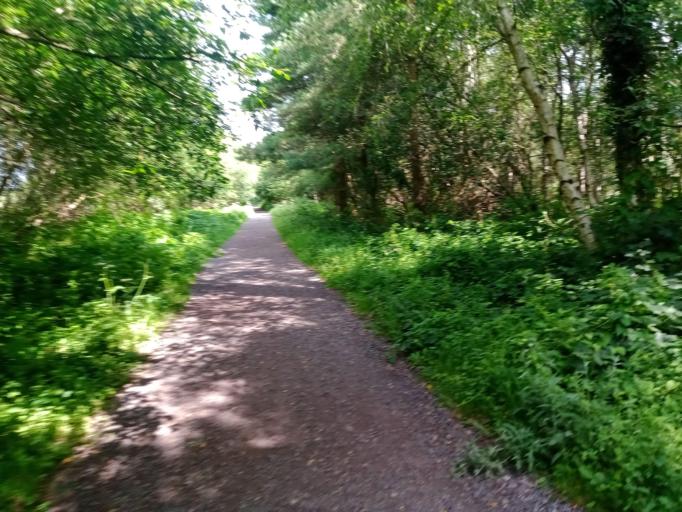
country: IE
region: Leinster
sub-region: Laois
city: Abbeyleix
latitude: 52.8975
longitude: -7.3501
